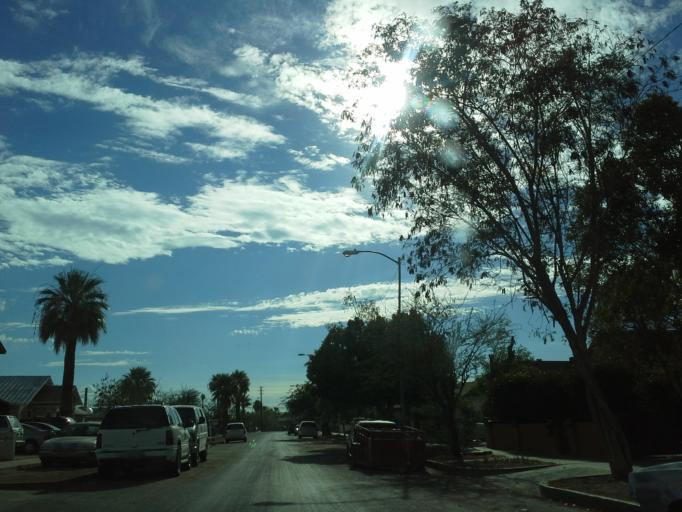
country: US
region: Arizona
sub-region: Maricopa County
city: Phoenix
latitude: 33.4543
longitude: -112.0893
